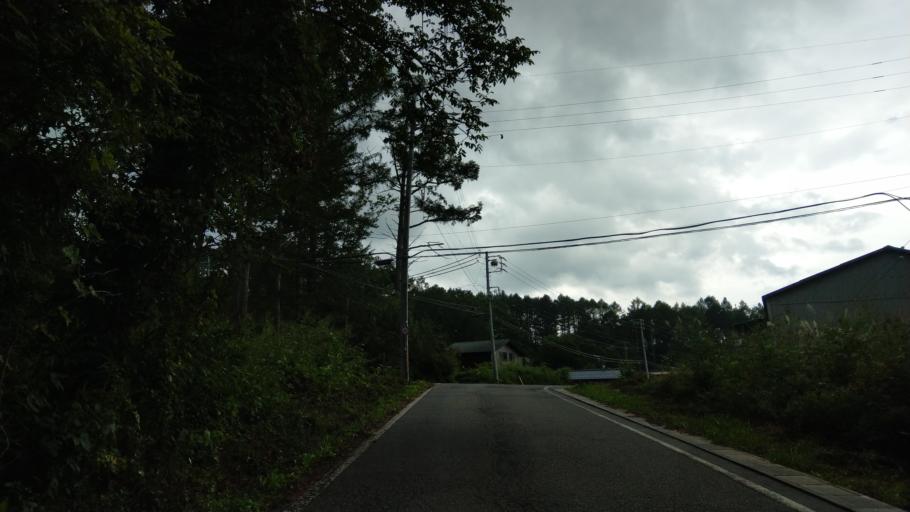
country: JP
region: Nagano
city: Komoro
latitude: 36.3053
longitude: 138.3907
